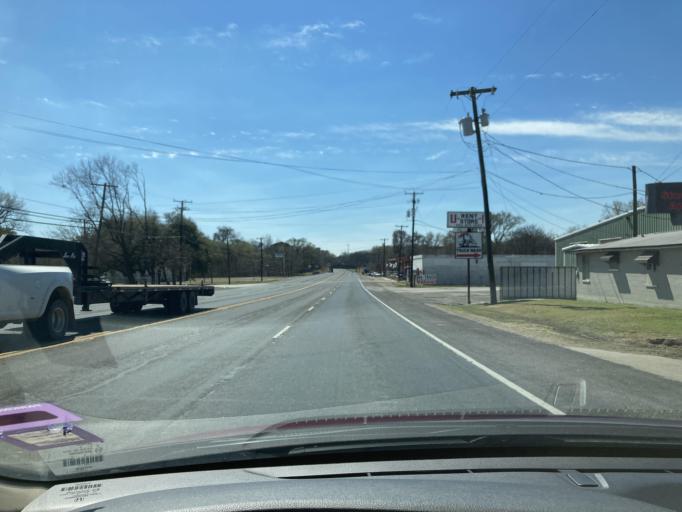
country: US
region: Texas
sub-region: Navarro County
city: Corsicana
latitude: 32.1059
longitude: -96.4635
